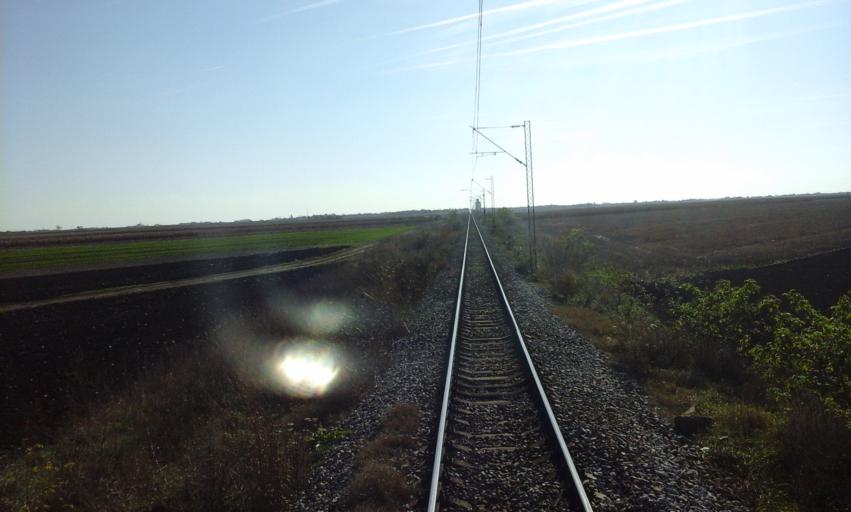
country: RS
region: Autonomna Pokrajina Vojvodina
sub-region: Severnobacki Okrug
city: Subotica
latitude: 45.9713
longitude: 19.6732
